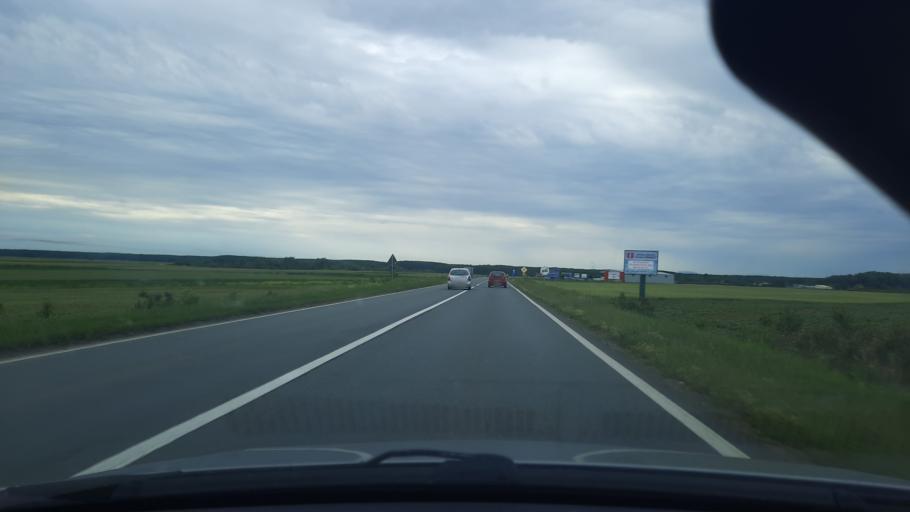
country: RS
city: Klenak
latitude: 44.7723
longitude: 19.7257
